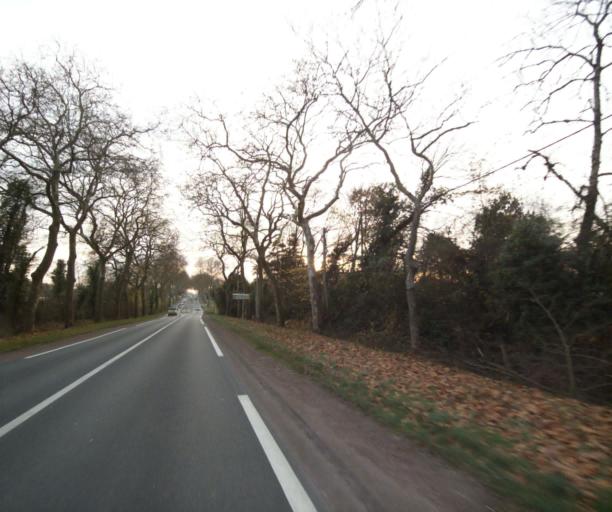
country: FR
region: Poitou-Charentes
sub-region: Departement de la Charente-Maritime
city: Fontcouverte
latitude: 45.7646
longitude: -0.5846
